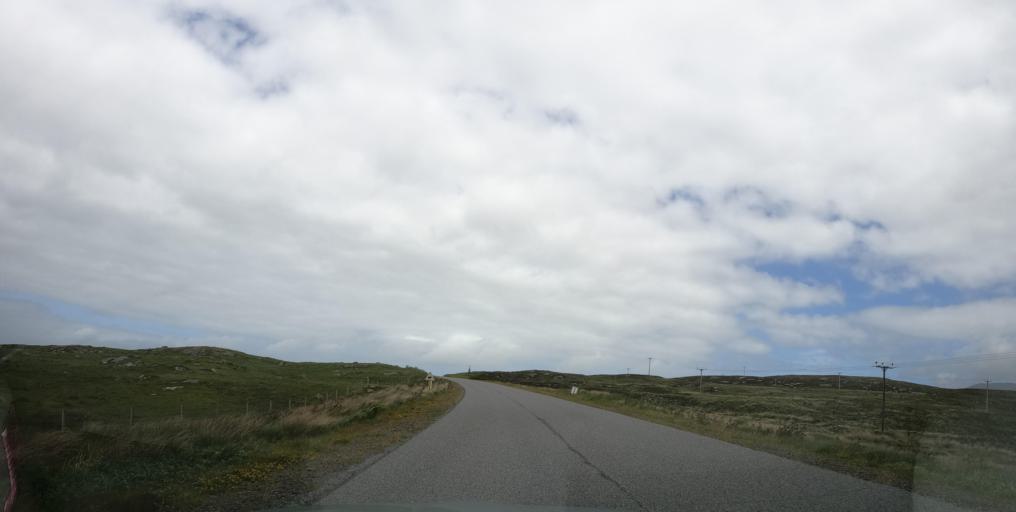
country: GB
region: Scotland
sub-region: Eilean Siar
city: Isle of South Uist
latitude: 57.2302
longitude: -7.3971
